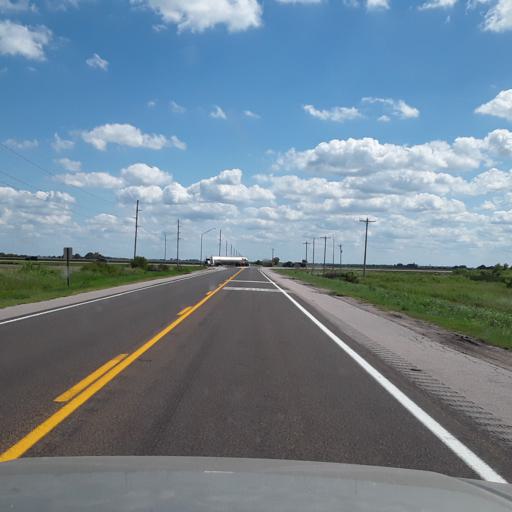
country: US
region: Nebraska
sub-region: Merrick County
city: Central City
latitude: 41.1935
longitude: -97.9829
